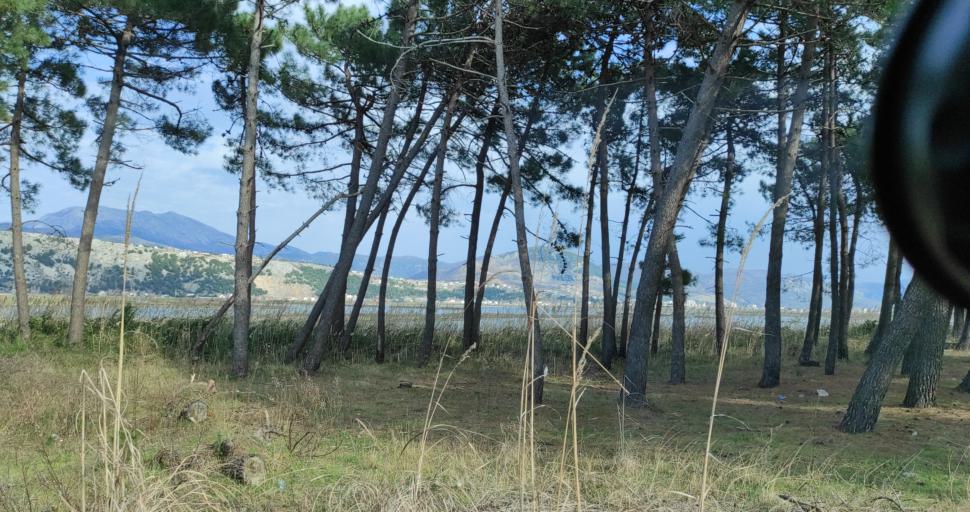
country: AL
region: Lezhe
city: Shengjin
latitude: 41.7861
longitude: 19.6036
